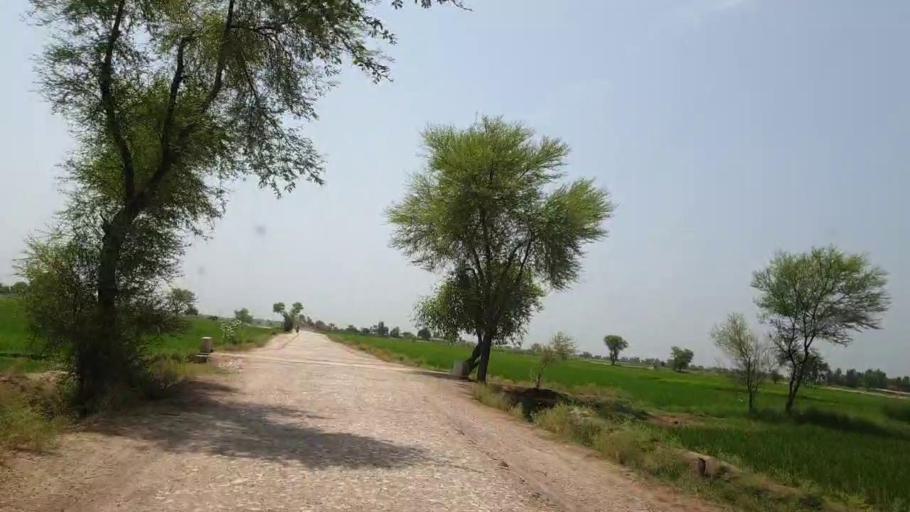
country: PK
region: Sindh
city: Shikarpur
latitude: 27.9137
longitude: 68.6339
